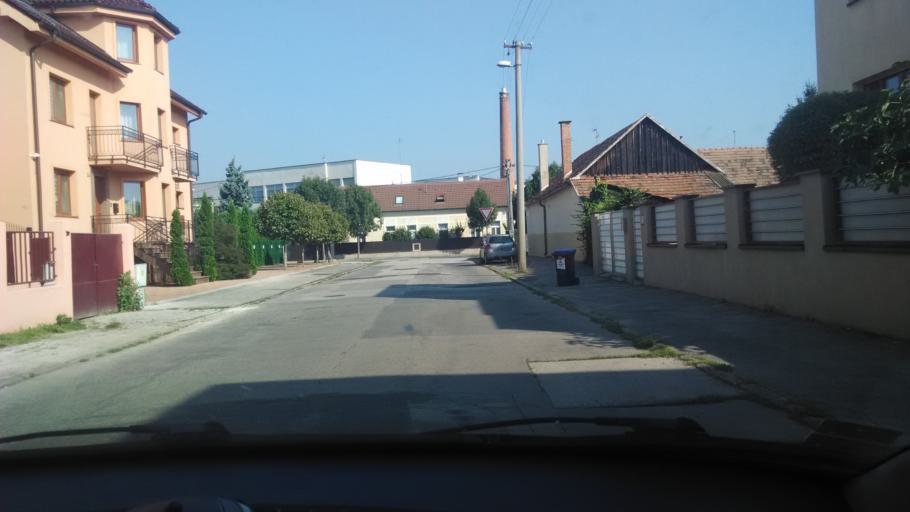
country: SK
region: Trnavsky
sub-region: Okres Trnava
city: Piestany
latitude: 48.5886
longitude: 17.8269
